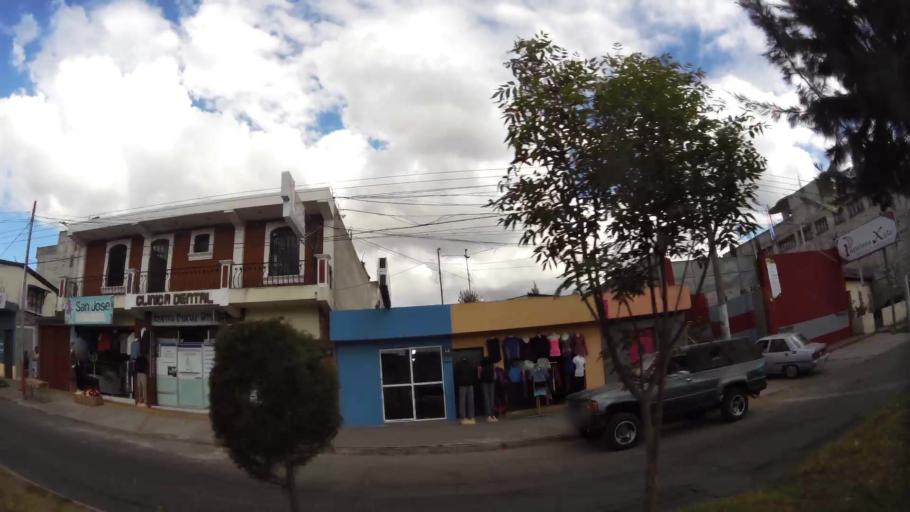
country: GT
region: Quetzaltenango
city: Quetzaltenango
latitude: 14.8426
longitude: -91.5254
